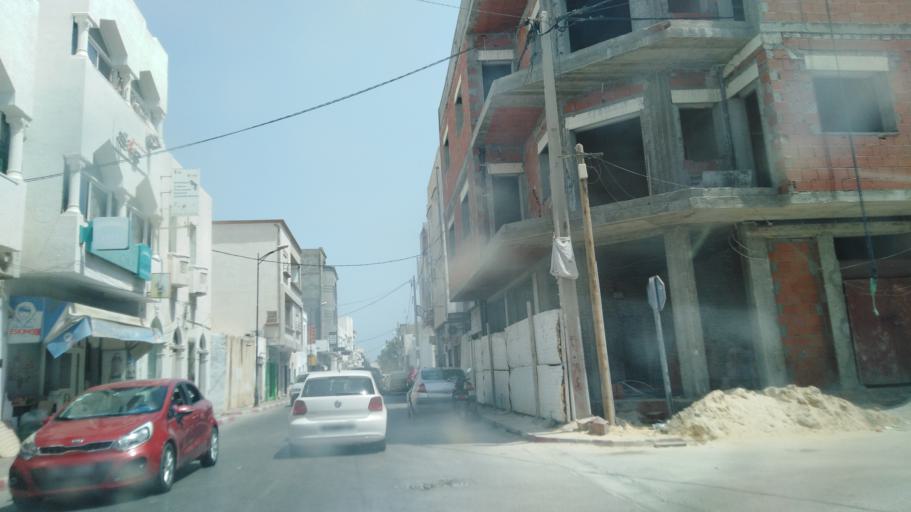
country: TN
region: Al Mahdiyah
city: Mahdia
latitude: 35.5070
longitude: 11.0580
